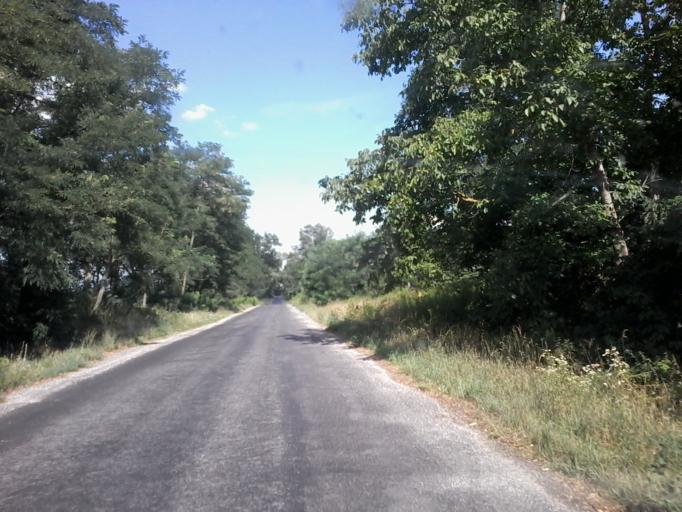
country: HU
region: Zala
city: Turje
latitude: 47.0517
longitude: 17.1280
